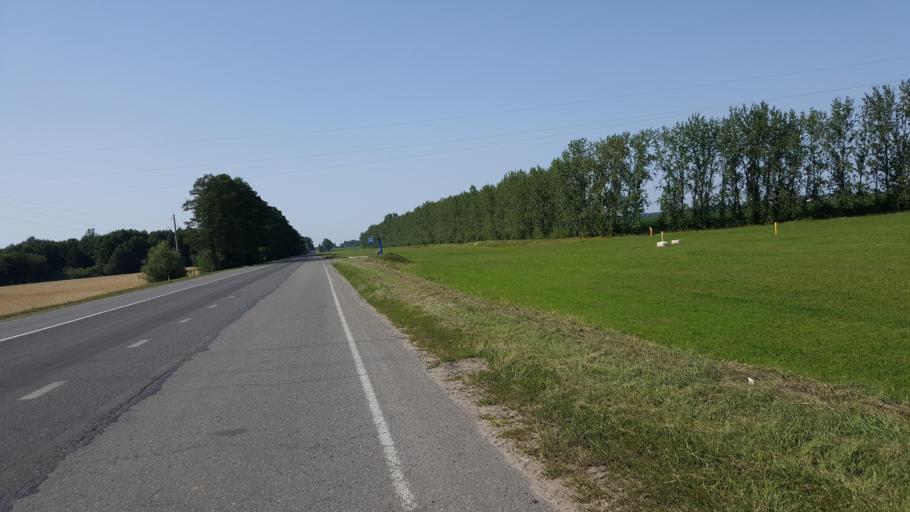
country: BY
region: Brest
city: Zhabinka
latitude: 52.2118
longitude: 23.9998
